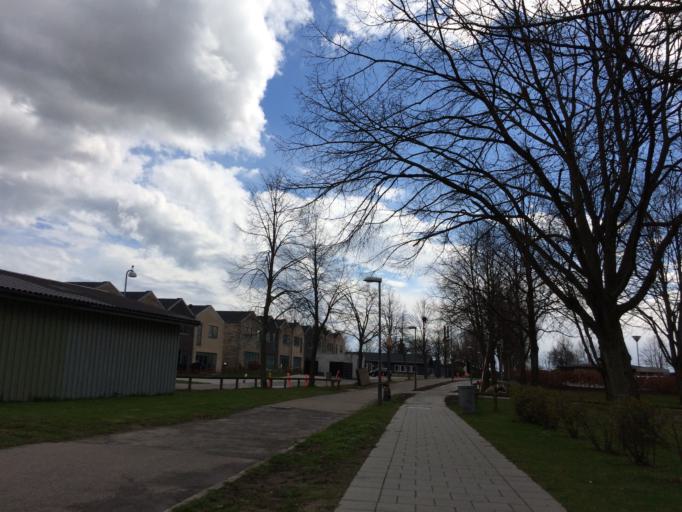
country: DK
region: Capital Region
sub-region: Hoje-Taastrup Kommune
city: Taastrup
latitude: 55.6433
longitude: 12.2869
